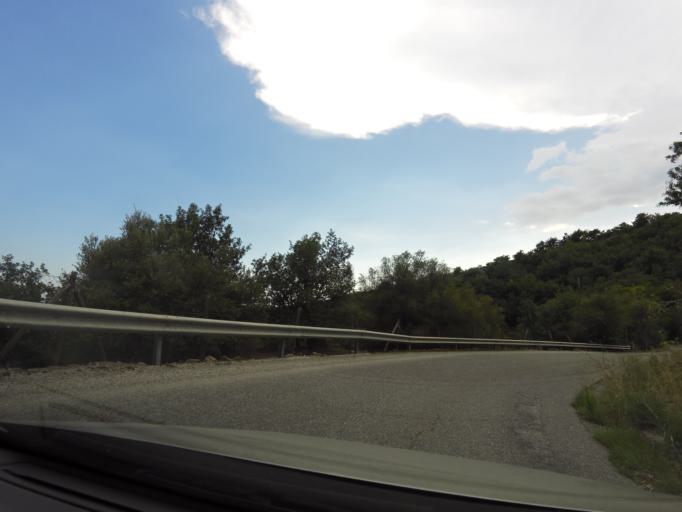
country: IT
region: Calabria
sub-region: Provincia di Reggio Calabria
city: Camini
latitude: 38.4360
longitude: 16.5146
